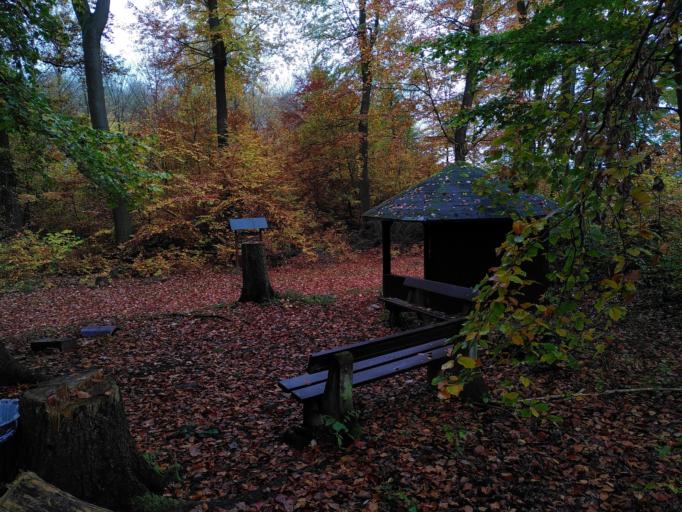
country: DE
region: Rheinland-Pfalz
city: Rengsdorf
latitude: 50.5051
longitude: 7.5034
